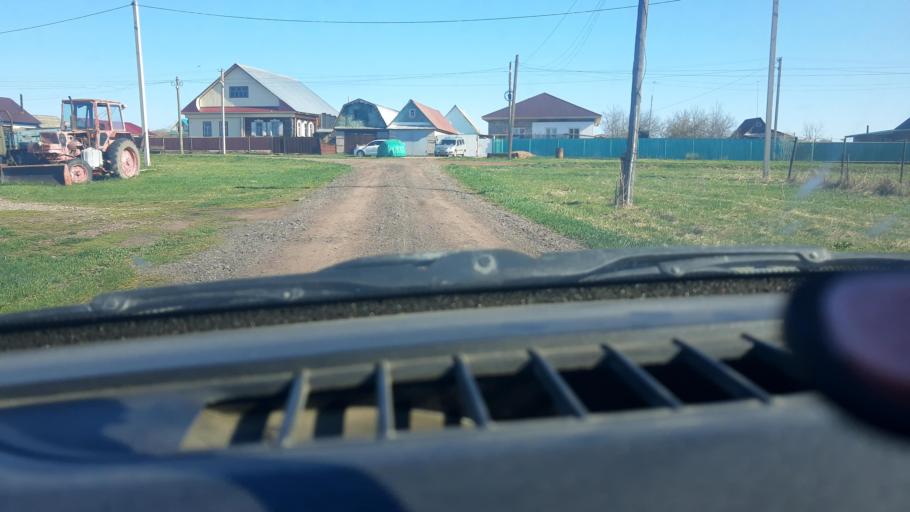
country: RU
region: Bashkortostan
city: Chishmy
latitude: 54.5966
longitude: 55.2703
